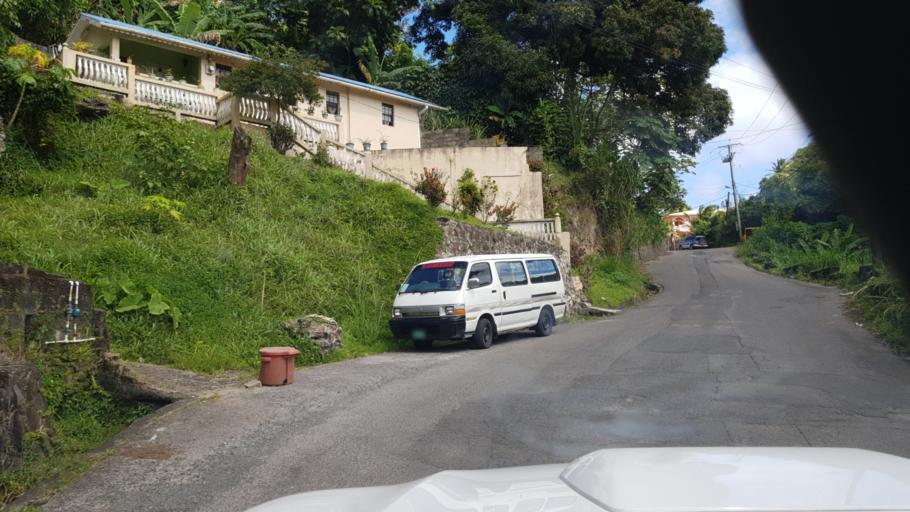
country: LC
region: Castries Quarter
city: Bisee
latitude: 13.9941
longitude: -60.9744
